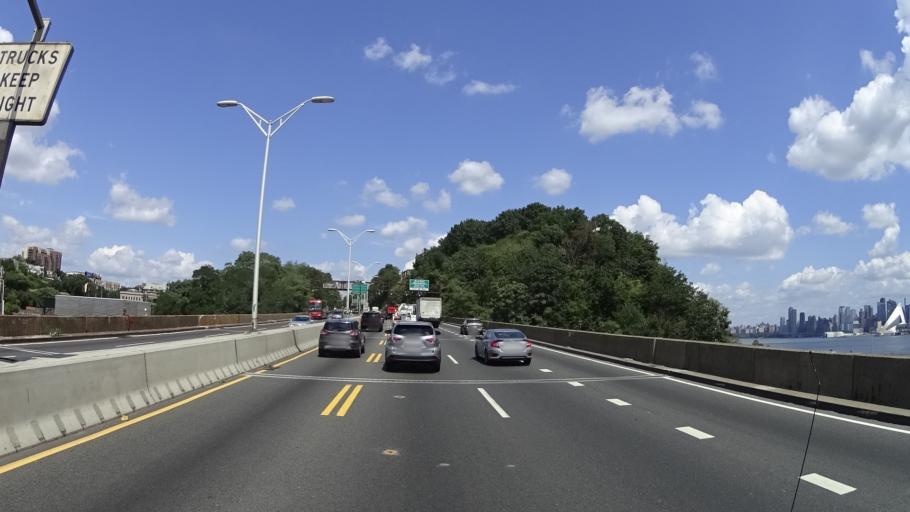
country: US
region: New Jersey
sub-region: Hudson County
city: Weehawken
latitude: 40.7638
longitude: -74.0222
